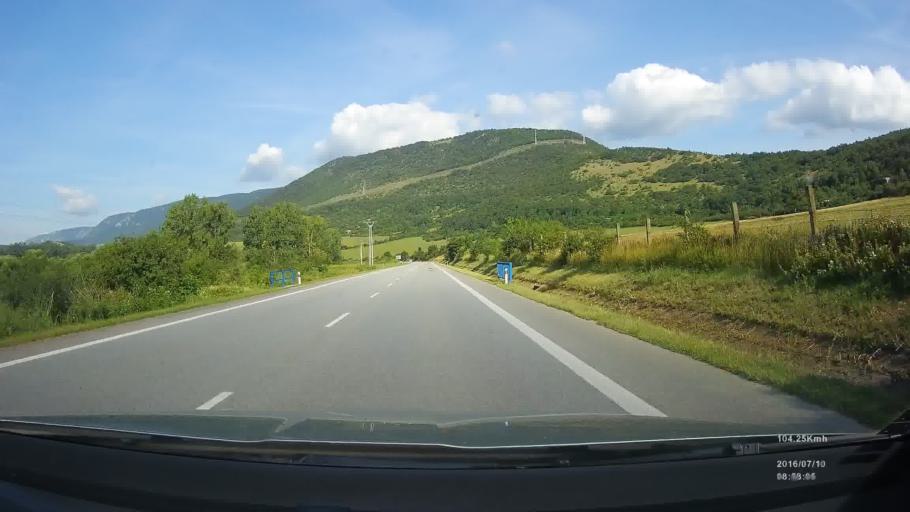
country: SK
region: Kosicky
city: Medzev
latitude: 48.6072
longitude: 20.8690
